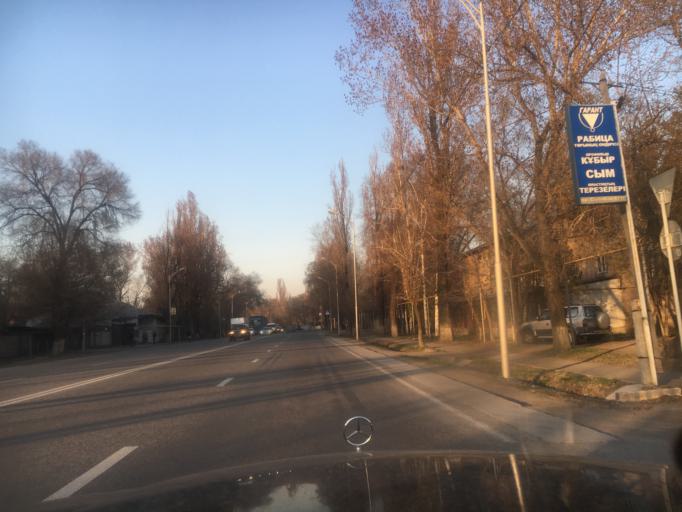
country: KZ
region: Almaty Oblysy
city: Pervomayskiy
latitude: 43.3530
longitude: 76.9746
